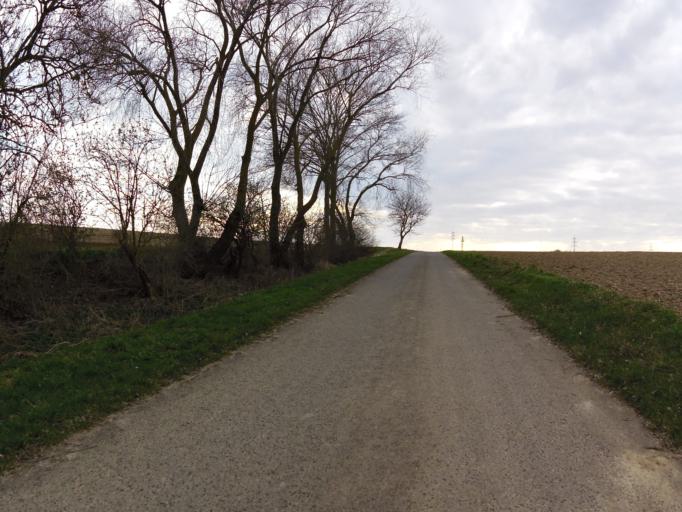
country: DE
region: Bavaria
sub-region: Regierungsbezirk Unterfranken
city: Buchbrunn
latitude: 49.7425
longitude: 10.1149
